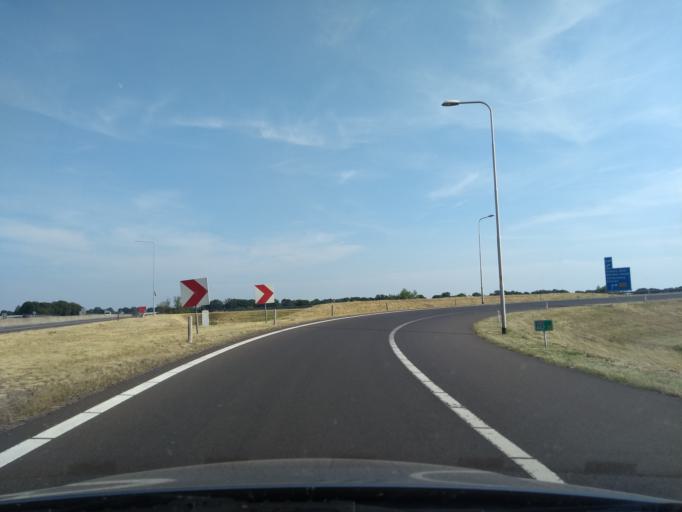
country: NL
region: Overijssel
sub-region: Gemeente Wierden
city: Wierden
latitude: 52.3414
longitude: 6.5968
